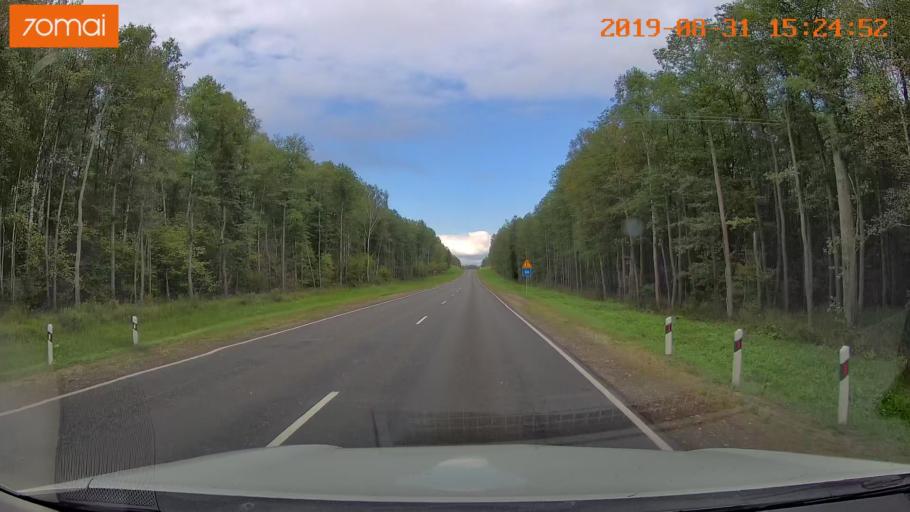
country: RU
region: Kaluga
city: Baryatino
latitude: 54.5336
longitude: 34.5111
